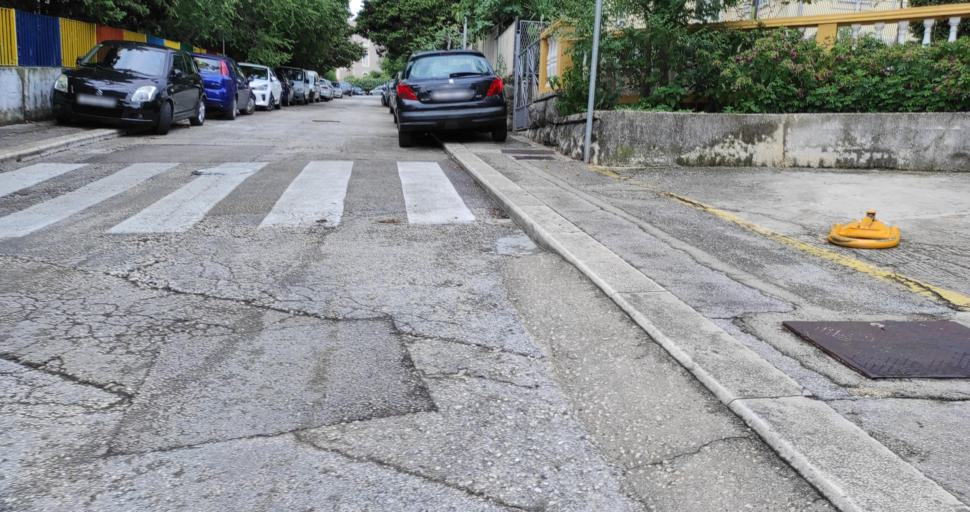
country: HR
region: Splitsko-Dalmatinska
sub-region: Grad Split
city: Split
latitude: 43.5118
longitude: 16.4288
